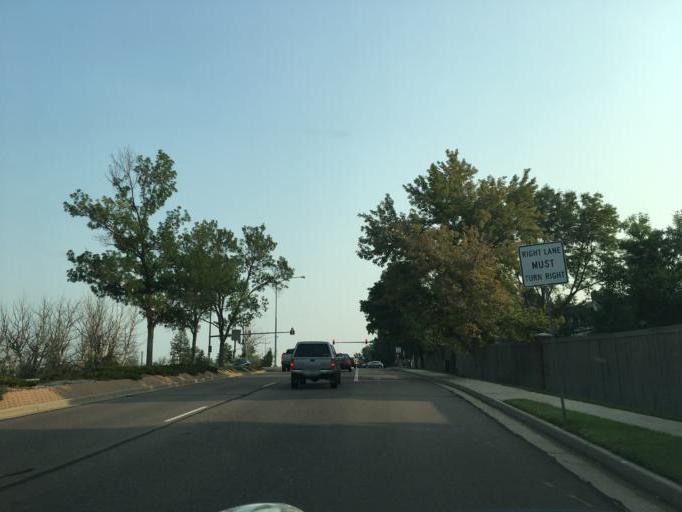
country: US
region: Colorado
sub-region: Adams County
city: Westminster
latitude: 39.8786
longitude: -105.0531
